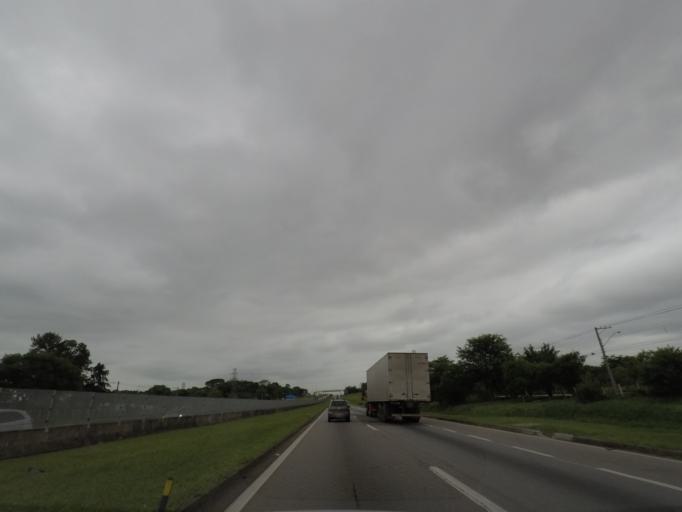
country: BR
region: Sao Paulo
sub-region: Sao Jose Dos Campos
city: Sao Jose dos Campos
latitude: -23.1703
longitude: -45.8214
